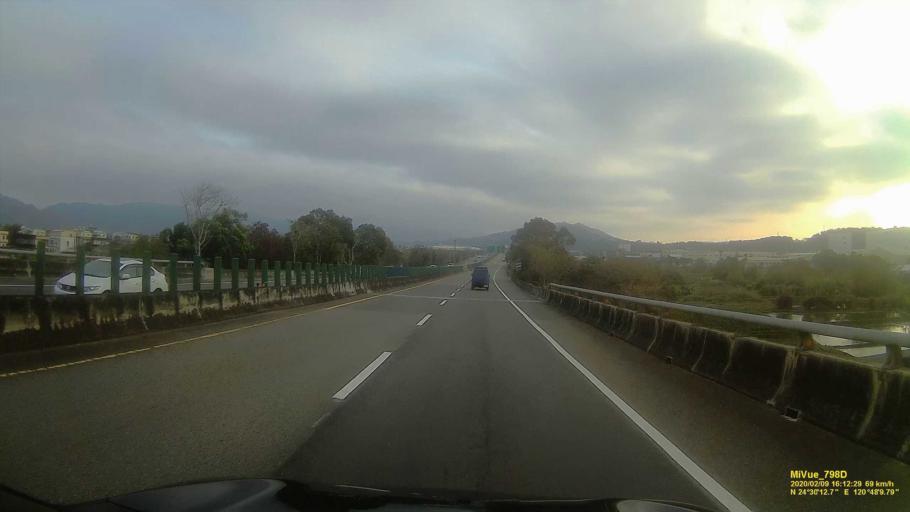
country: TW
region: Taiwan
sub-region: Miaoli
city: Miaoli
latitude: 24.5033
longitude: 120.8027
